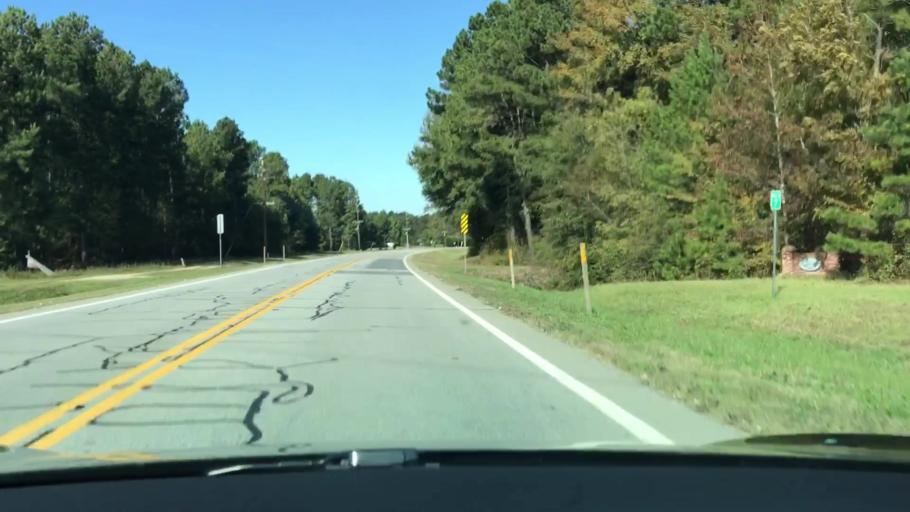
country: US
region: Georgia
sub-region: Warren County
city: Warrenton
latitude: 33.3908
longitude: -82.6459
